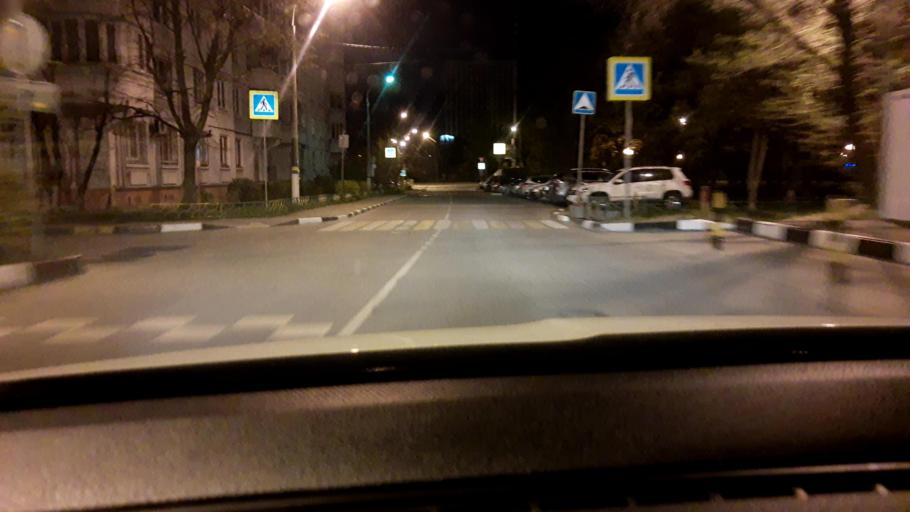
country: RU
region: Moskovskaya
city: Lyubertsy
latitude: 55.6631
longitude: 37.8695
